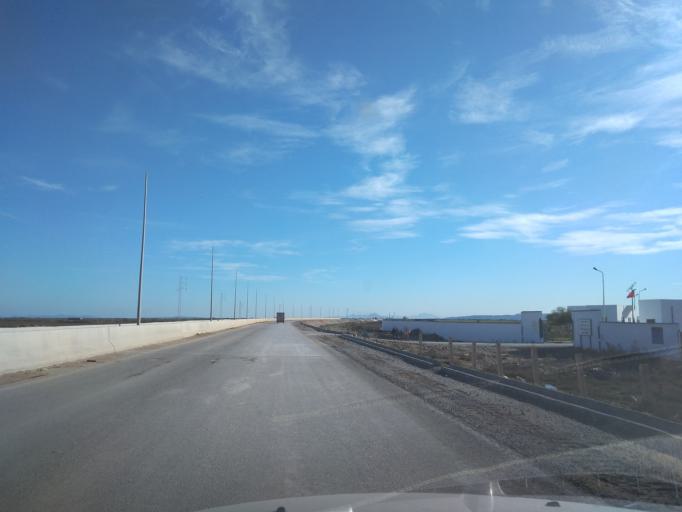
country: TN
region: Ariana
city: Qal'at al Andalus
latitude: 37.0411
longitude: 10.1304
